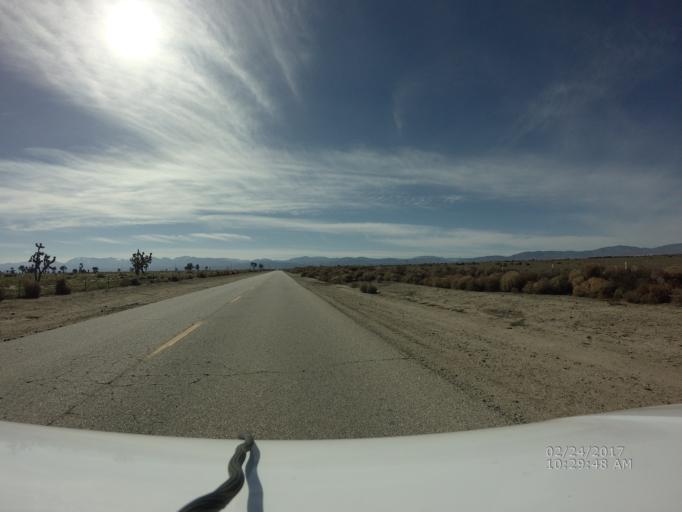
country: US
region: California
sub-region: Los Angeles County
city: Littlerock
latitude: 34.6372
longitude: -118.0053
